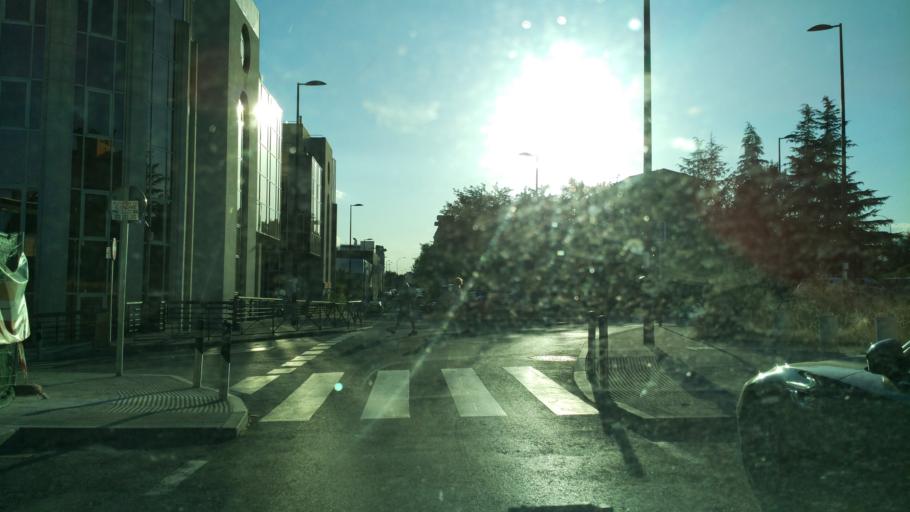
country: ES
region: Madrid
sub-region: Provincia de Madrid
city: Las Tablas
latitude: 40.4907
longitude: -3.6888
